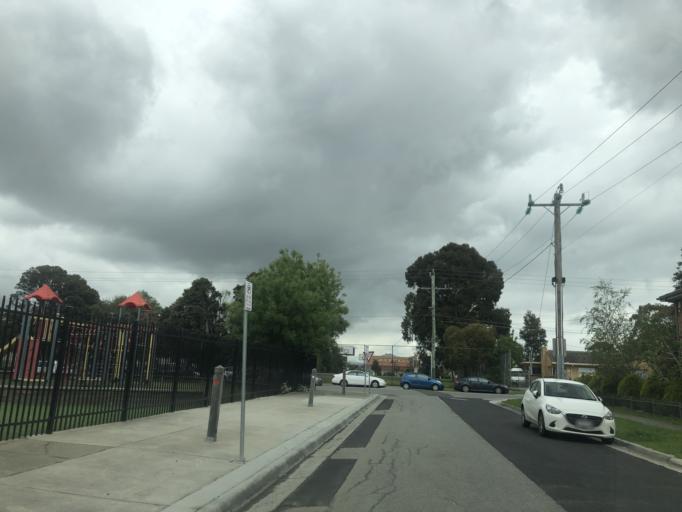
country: AU
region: Victoria
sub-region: Greater Dandenong
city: Dandenong North
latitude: -37.9762
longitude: 145.2132
